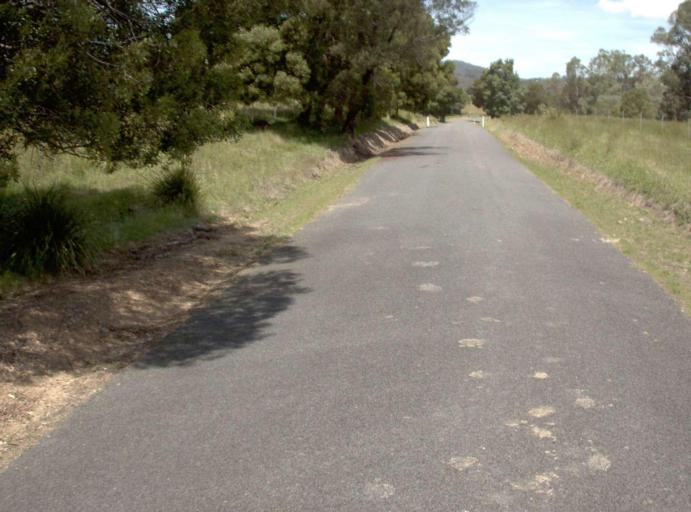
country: AU
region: New South Wales
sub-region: Bombala
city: Bombala
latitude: -37.4134
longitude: 149.0097
